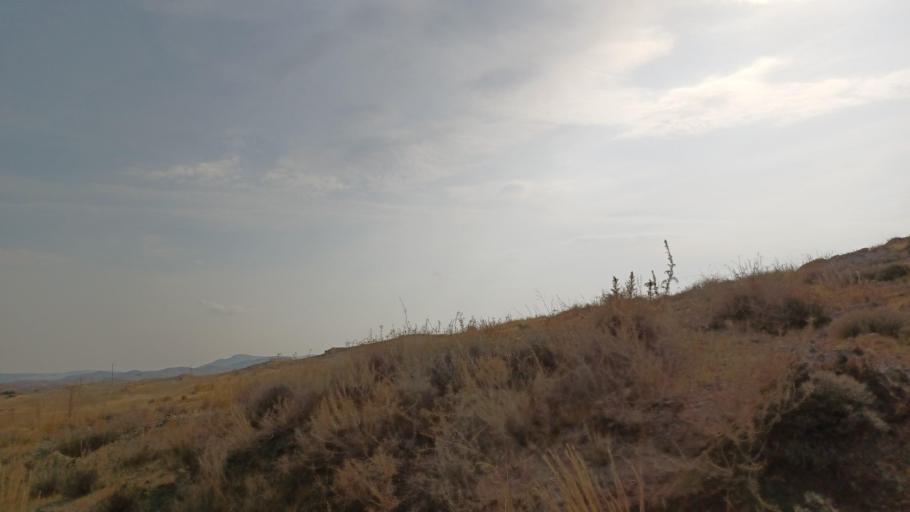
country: CY
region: Larnaka
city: Troulloi
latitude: 35.0143
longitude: 33.5797
